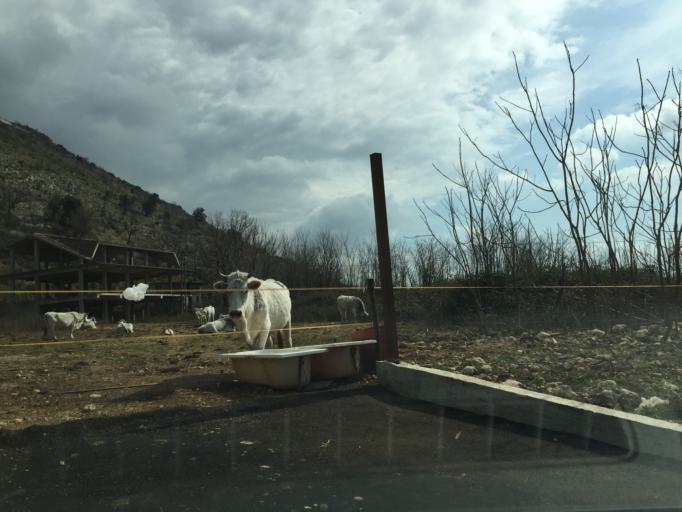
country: IT
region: Latium
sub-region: Provincia di Frosinone
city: Castrocielo
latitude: 41.5242
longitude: 13.7035
